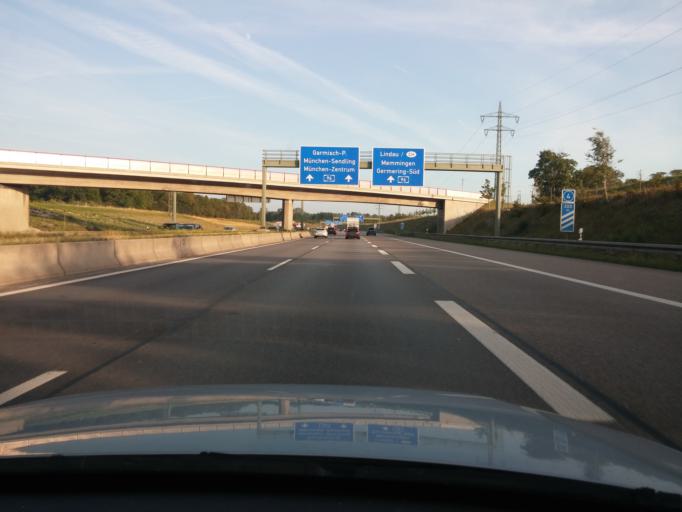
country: DE
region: Bavaria
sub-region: Upper Bavaria
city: Germering
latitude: 48.1338
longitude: 11.3994
